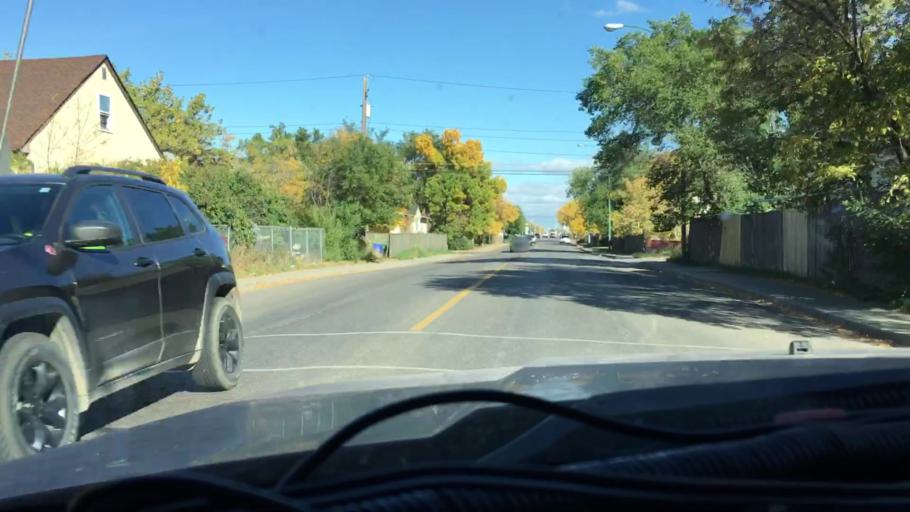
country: CA
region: Saskatchewan
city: Regina
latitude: 50.4629
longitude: -104.6239
